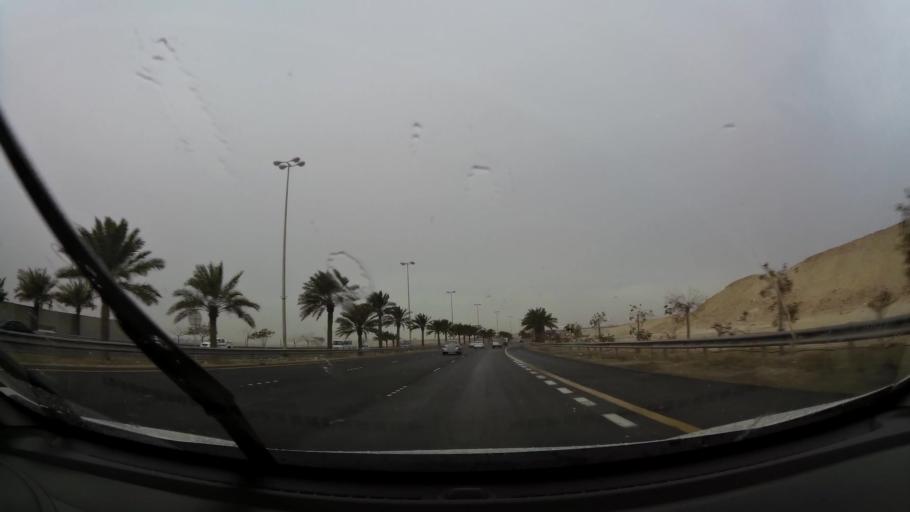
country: BH
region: Central Governorate
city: Dar Kulayb
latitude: 26.0905
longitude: 50.5150
